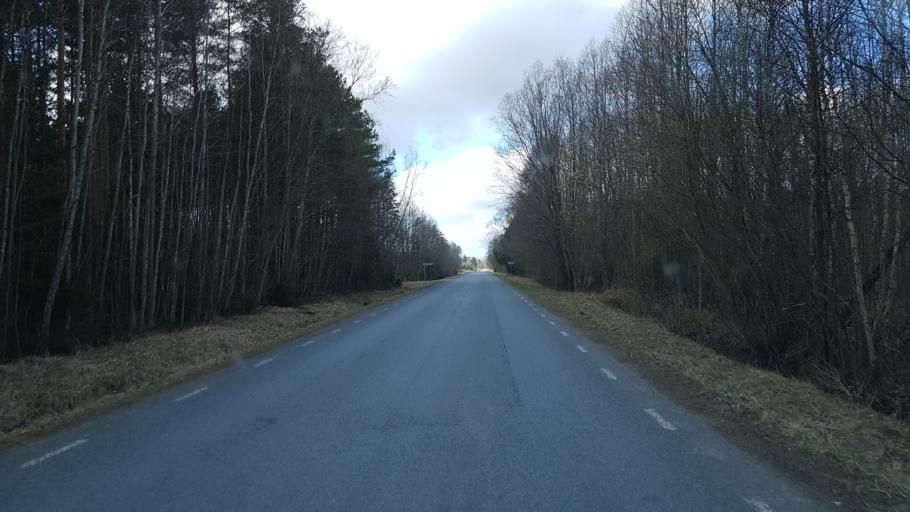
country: EE
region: Raplamaa
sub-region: Maerjamaa vald
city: Marjamaa
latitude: 58.7680
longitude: 24.4375
